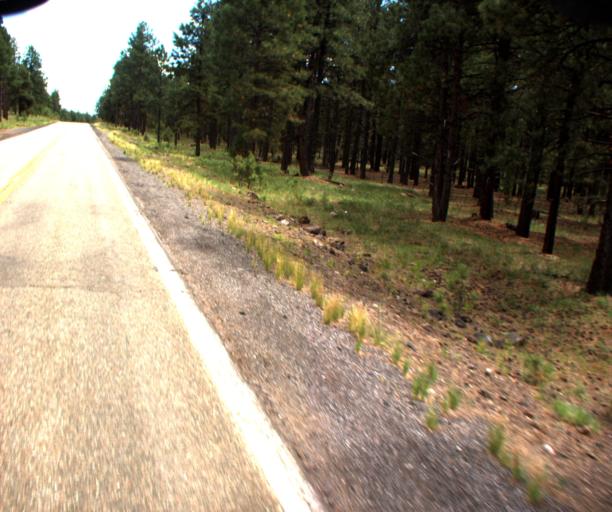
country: US
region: Arizona
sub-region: Coconino County
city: Flagstaff
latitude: 35.3083
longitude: -111.7730
